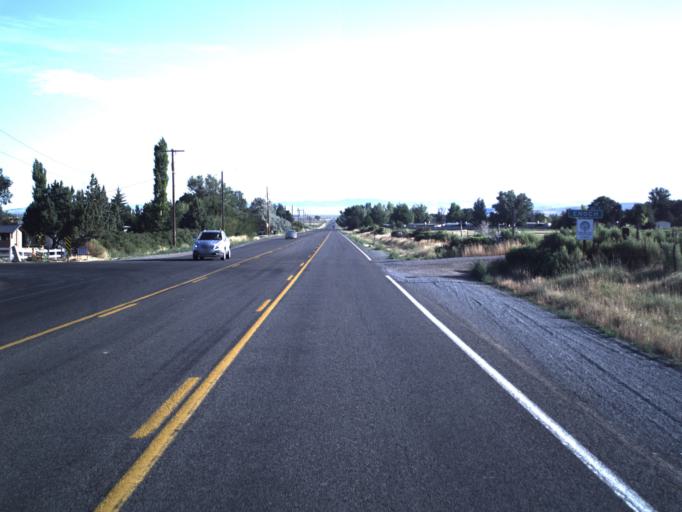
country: US
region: Utah
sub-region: Iron County
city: Enoch
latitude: 37.7427
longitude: -113.0552
